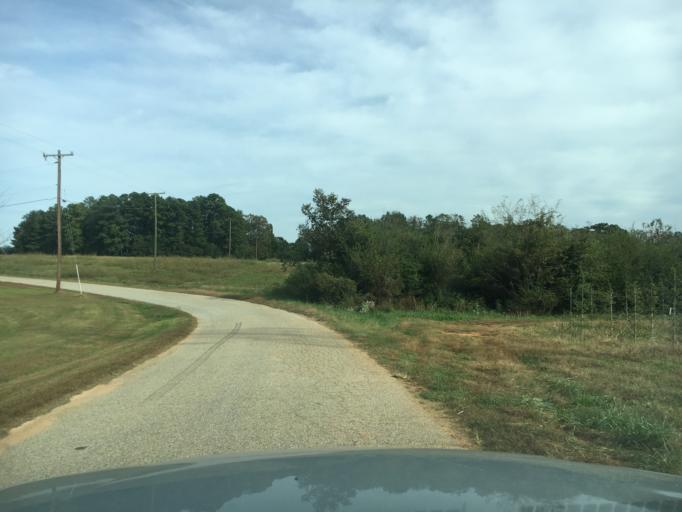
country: US
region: South Carolina
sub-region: Spartanburg County
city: Duncan
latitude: 34.9152
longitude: -82.1489
